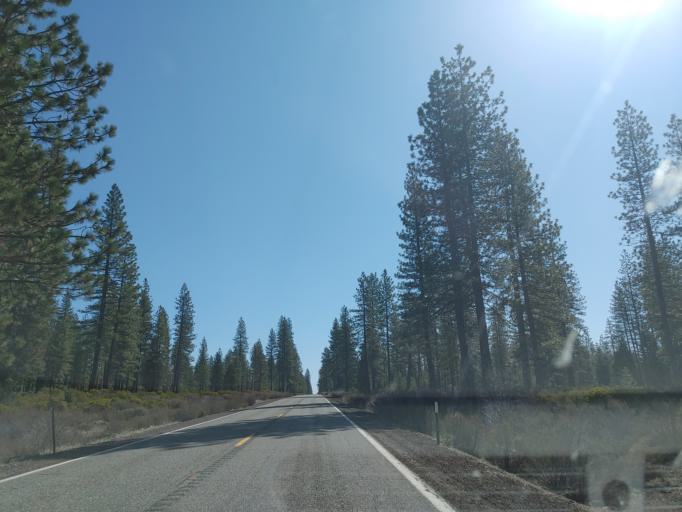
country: US
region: California
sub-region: Siskiyou County
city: McCloud
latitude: 41.2557
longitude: -122.0478
